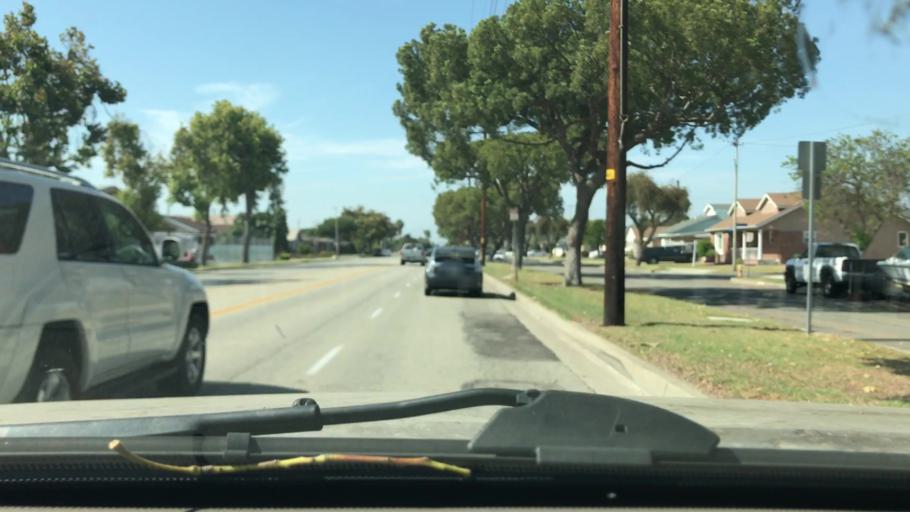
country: US
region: California
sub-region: Orange County
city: Rossmoor
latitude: 33.7989
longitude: -118.1079
